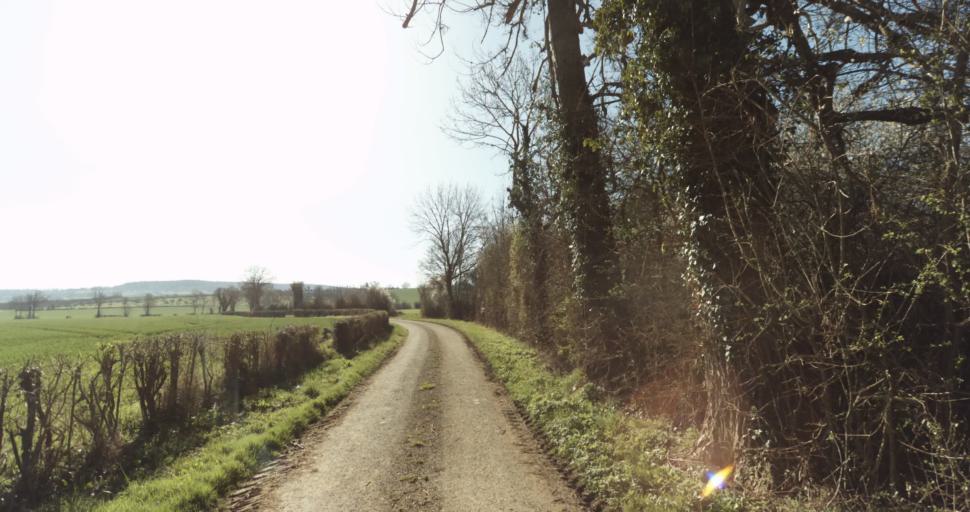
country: FR
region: Lower Normandy
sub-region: Departement du Calvados
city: Saint-Pierre-sur-Dives
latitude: 48.9539
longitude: 0.0184
